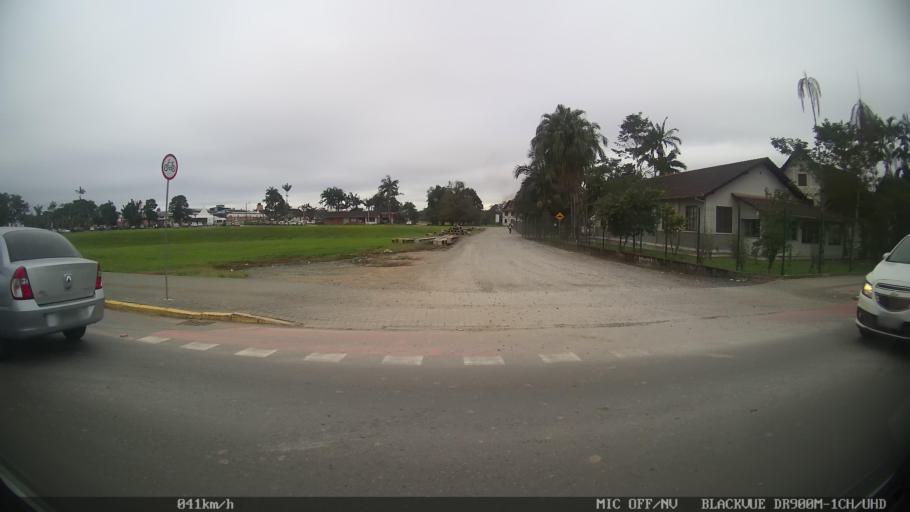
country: BR
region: Santa Catarina
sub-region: Joinville
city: Joinville
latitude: -26.2054
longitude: -48.9074
